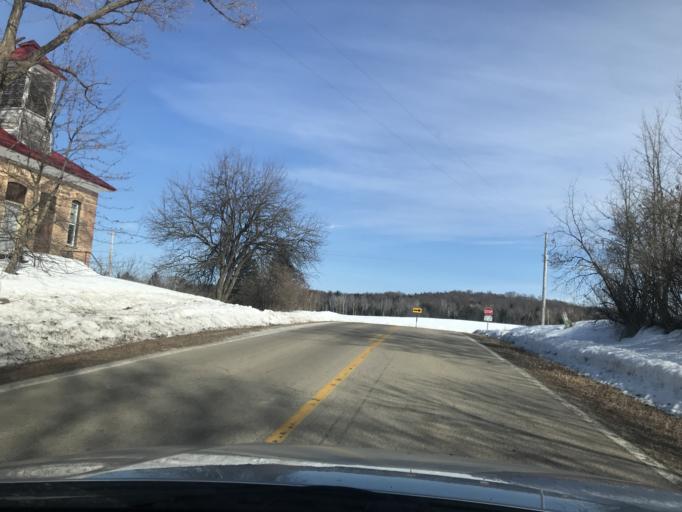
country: US
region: Wisconsin
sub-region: Oconto County
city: Gillett
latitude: 44.9606
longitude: -88.2651
